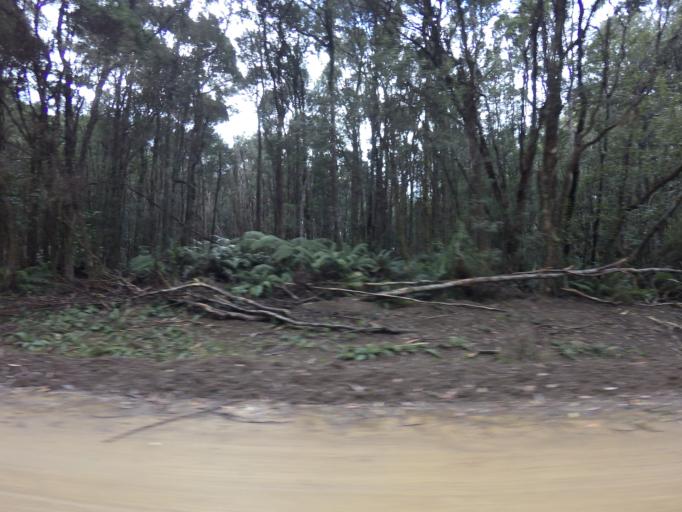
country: AU
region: Tasmania
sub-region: Huon Valley
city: Geeveston
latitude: -43.5578
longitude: 146.8902
